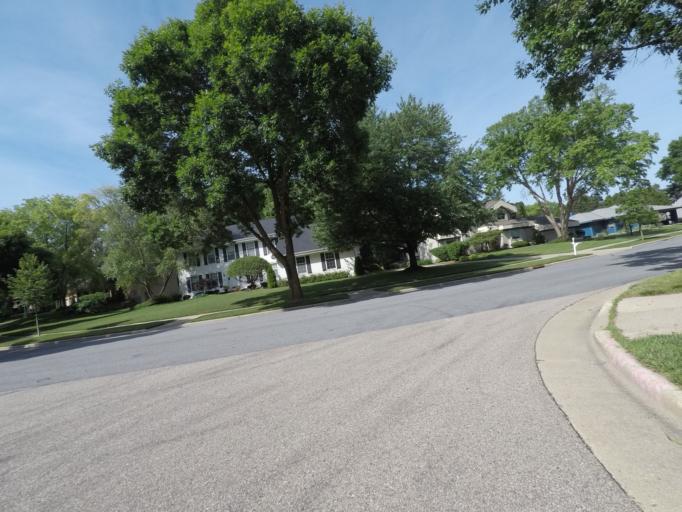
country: US
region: Wisconsin
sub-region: Dane County
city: Middleton
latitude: 43.0819
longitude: -89.4967
